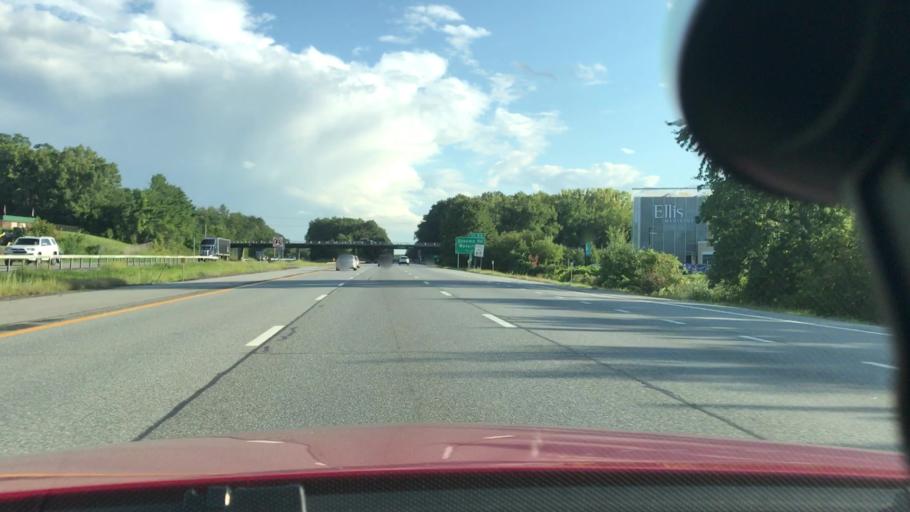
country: US
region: New York
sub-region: Saratoga County
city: Country Knolls
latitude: 42.8555
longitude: -73.7743
